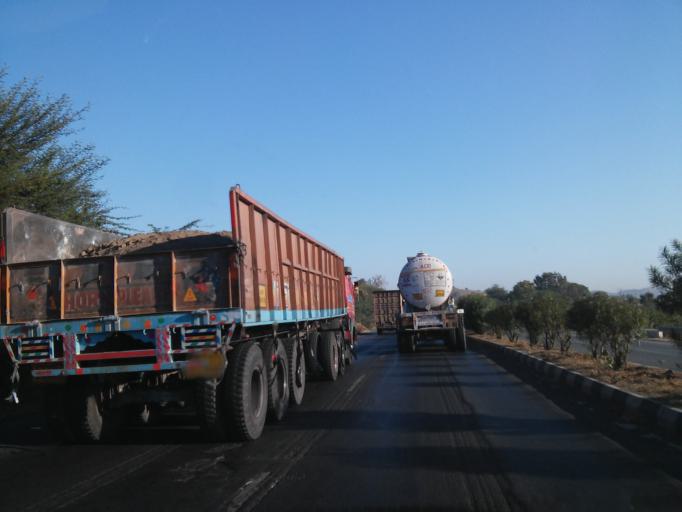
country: IN
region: Rajasthan
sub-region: Dungarpur
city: Dungarpur
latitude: 24.0068
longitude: 73.6558
